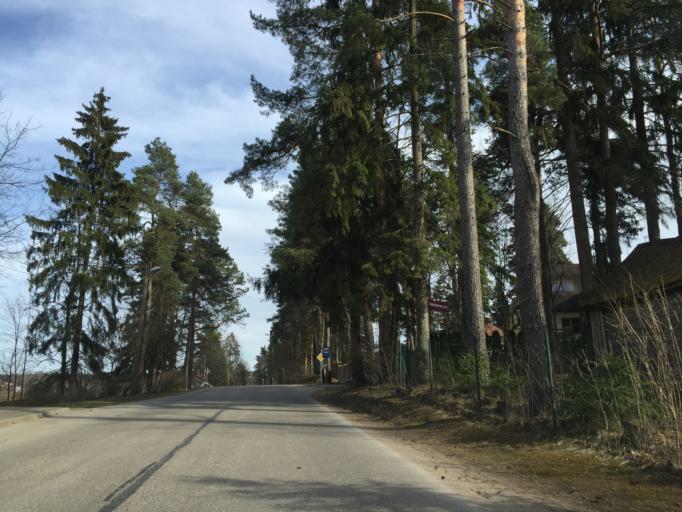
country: LV
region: Ogre
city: Ogre
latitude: 56.8112
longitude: 24.6281
